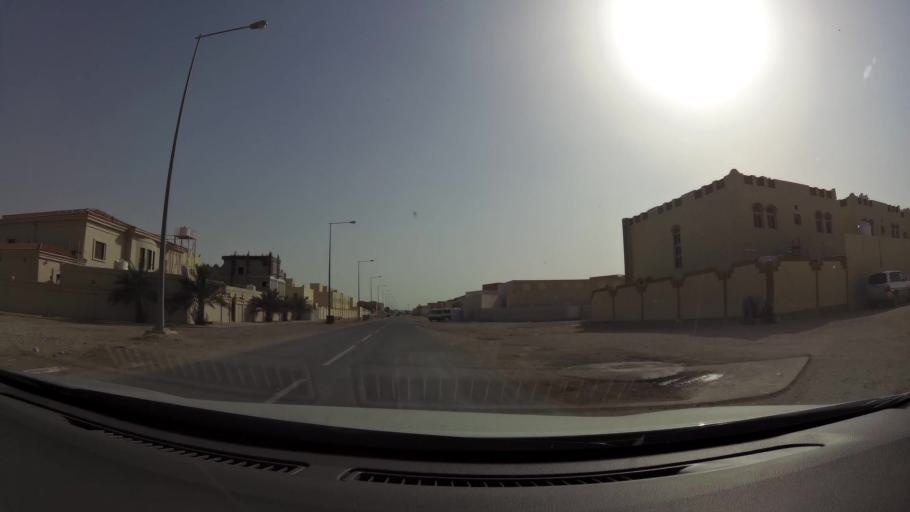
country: QA
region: Baladiyat ar Rayyan
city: Ar Rayyan
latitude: 25.3355
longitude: 51.4222
